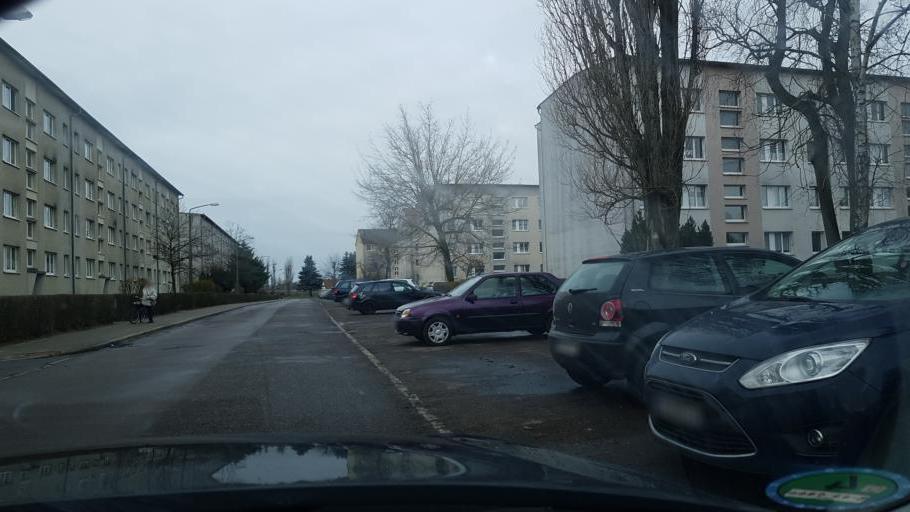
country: DE
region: Brandenburg
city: Kyritz
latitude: 52.9486
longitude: 12.3834
